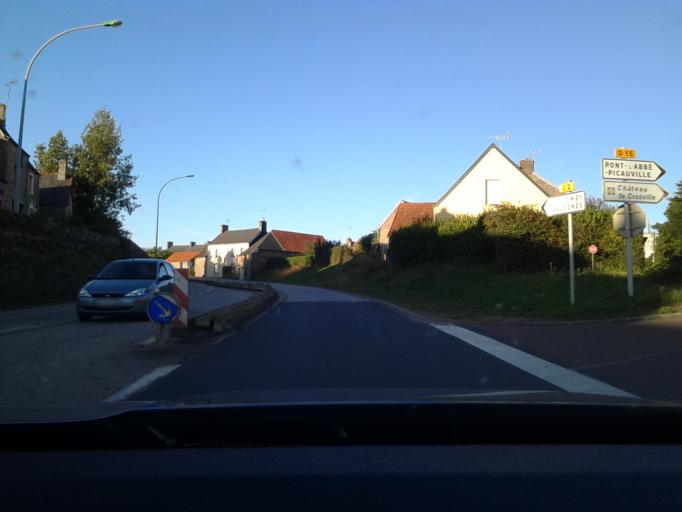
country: FR
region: Lower Normandy
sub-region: Departement de la Manche
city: Saint-Sauveur-le-Vicomte
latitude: 49.3915
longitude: -1.5208
